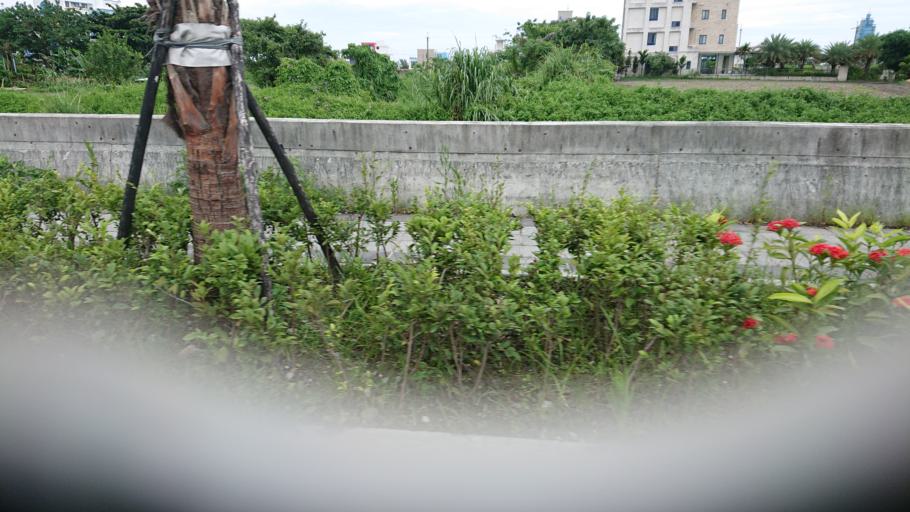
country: TW
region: Taiwan
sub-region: Hualien
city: Hualian
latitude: 23.9566
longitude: 121.6022
